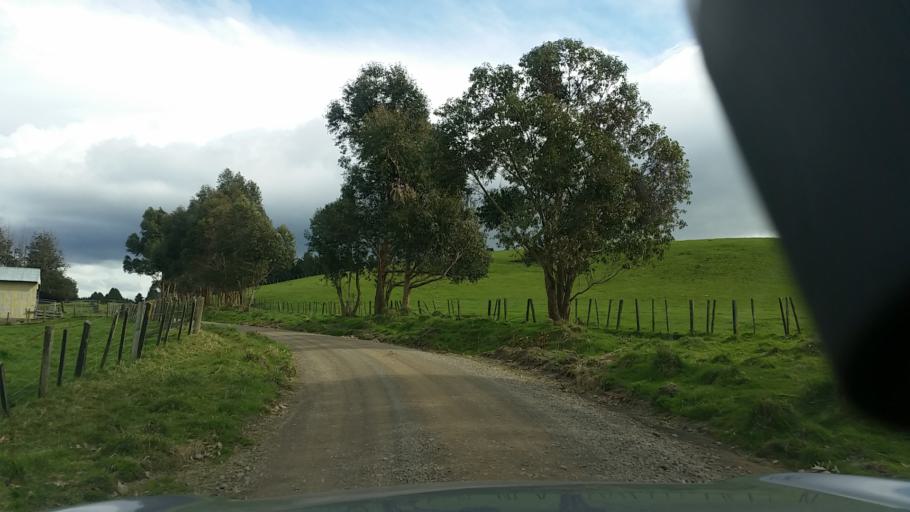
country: NZ
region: Hawke's Bay
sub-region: Napier City
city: Napier
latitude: -39.2045
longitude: 176.9279
